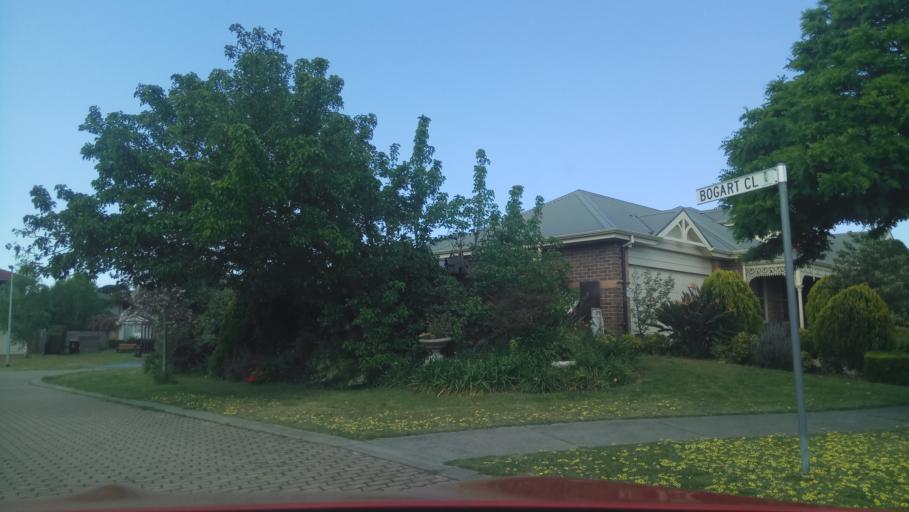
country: AU
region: Victoria
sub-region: Kingston
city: Dingley Village
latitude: -37.9720
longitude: 145.1244
